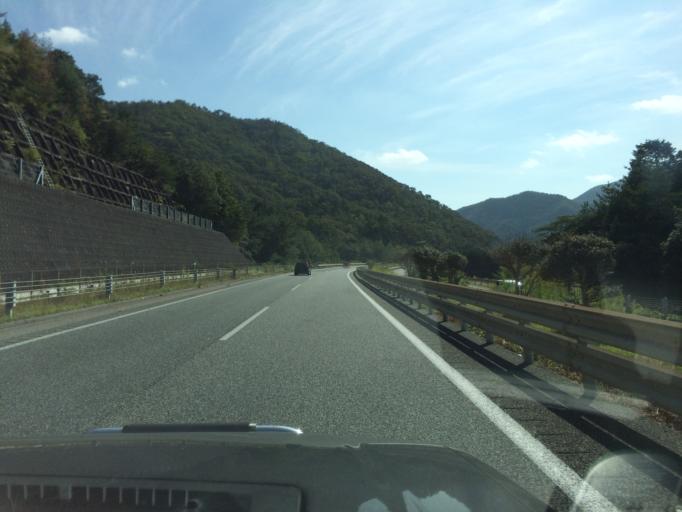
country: JP
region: Hyogo
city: Sasayama
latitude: 35.0060
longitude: 135.1591
